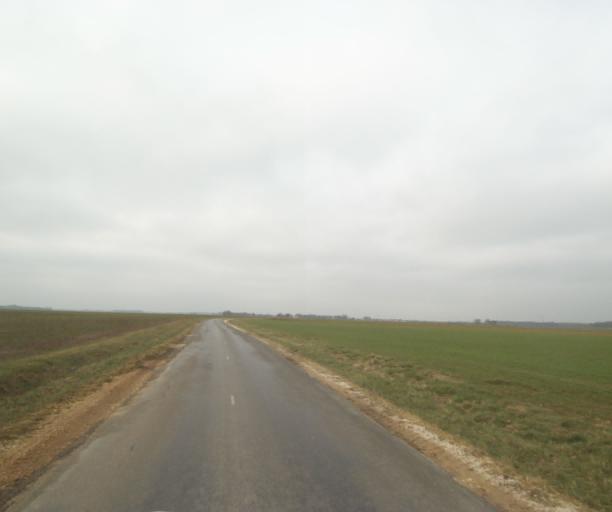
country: FR
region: Champagne-Ardenne
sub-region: Departement de la Haute-Marne
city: Villiers-en-Lieu
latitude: 48.6773
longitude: 4.8577
